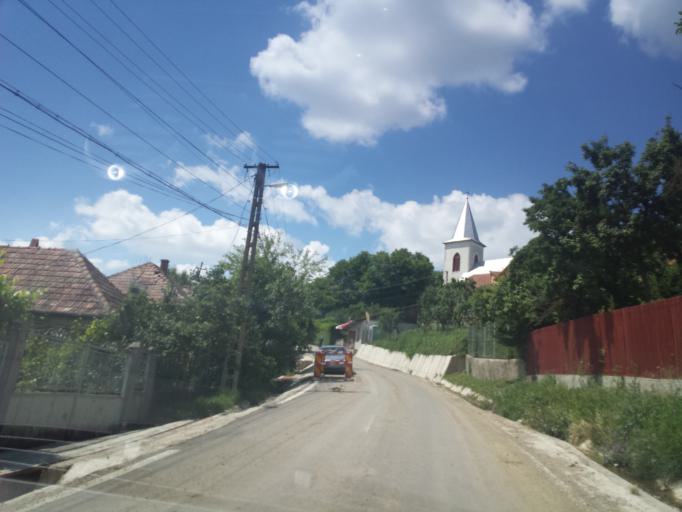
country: RO
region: Cluj
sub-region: Comuna Apahida
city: Dezmir
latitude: 46.7651
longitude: 23.7241
